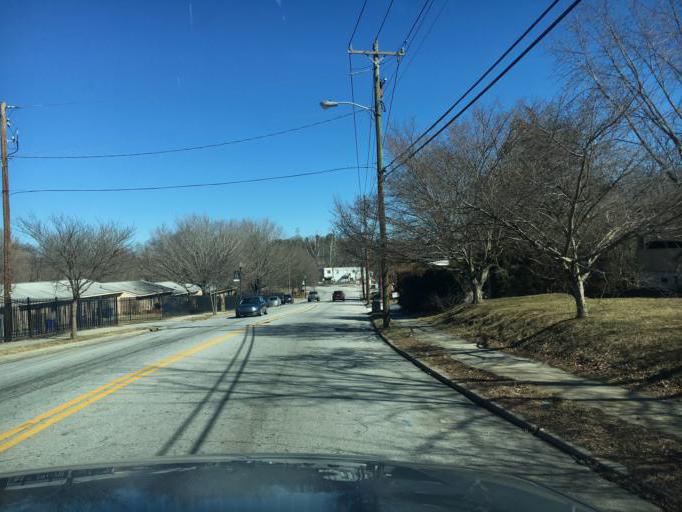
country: US
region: North Carolina
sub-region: Henderson County
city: Hendersonville
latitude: 35.3235
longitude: -82.4546
